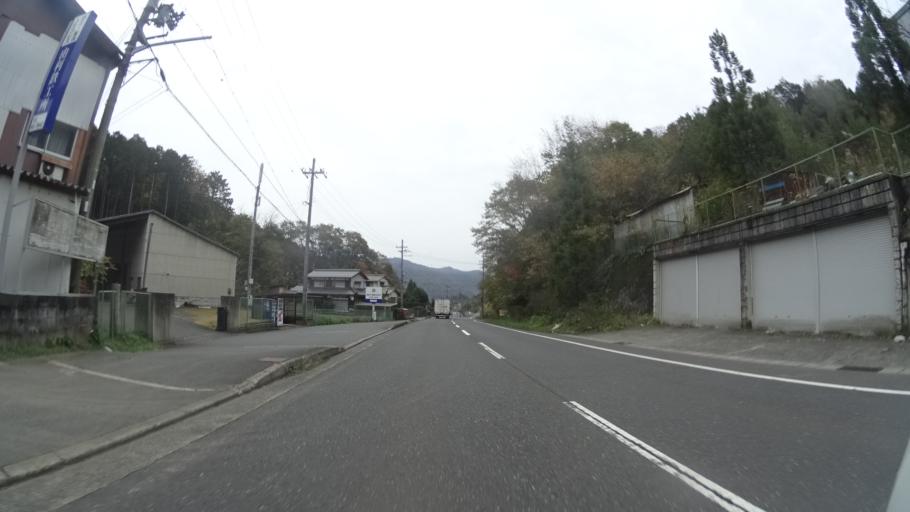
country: JP
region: Kyoto
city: Maizuru
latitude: 35.4688
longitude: 135.4237
